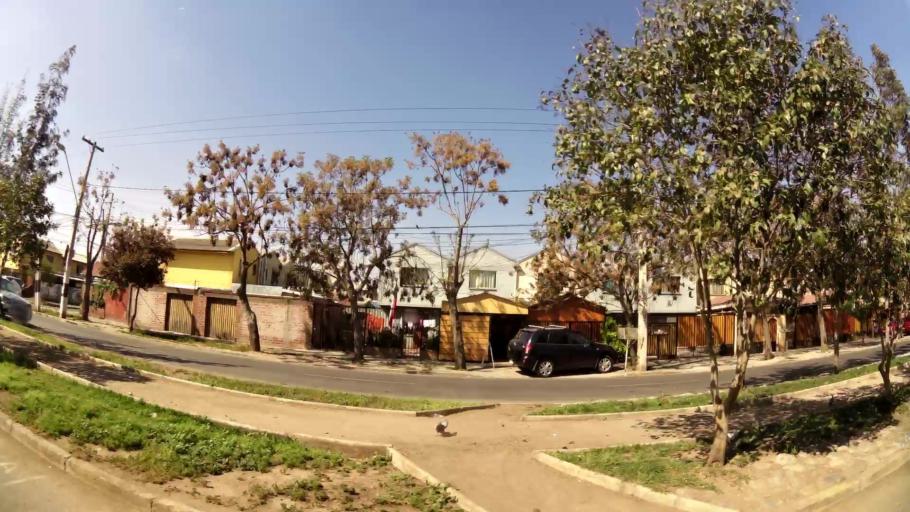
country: CL
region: Santiago Metropolitan
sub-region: Provincia de Santiago
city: La Pintana
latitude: -33.5642
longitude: -70.6224
